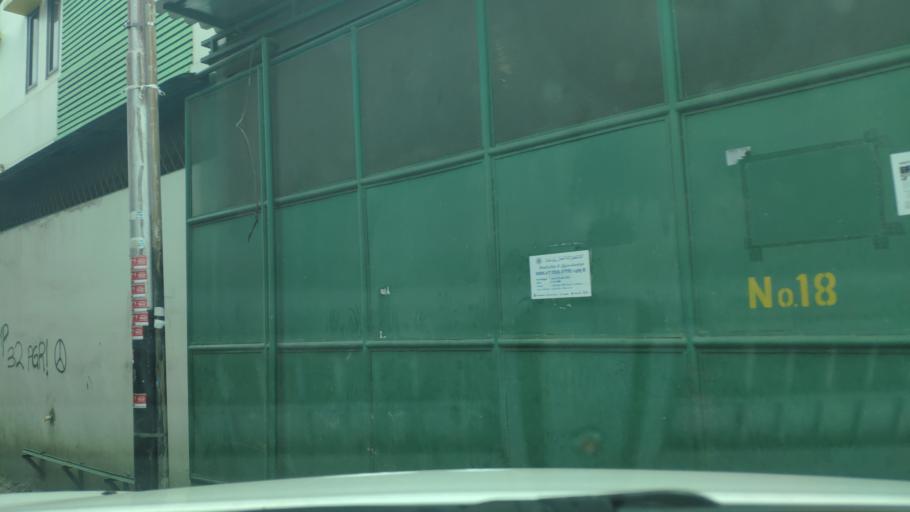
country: ID
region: Jakarta Raya
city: Jakarta
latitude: -6.1488
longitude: 106.8186
